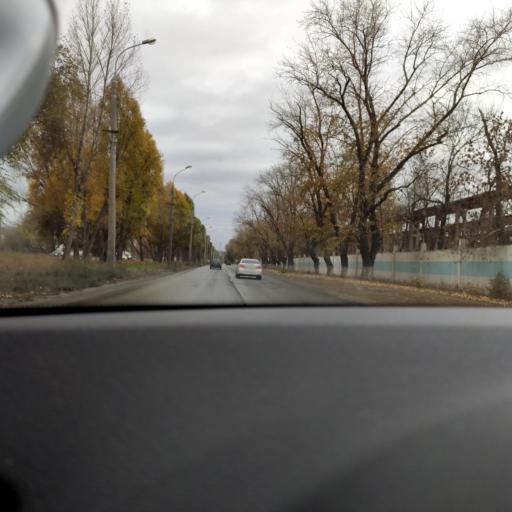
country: RU
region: Samara
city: Petra-Dubrava
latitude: 53.2425
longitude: 50.3083
